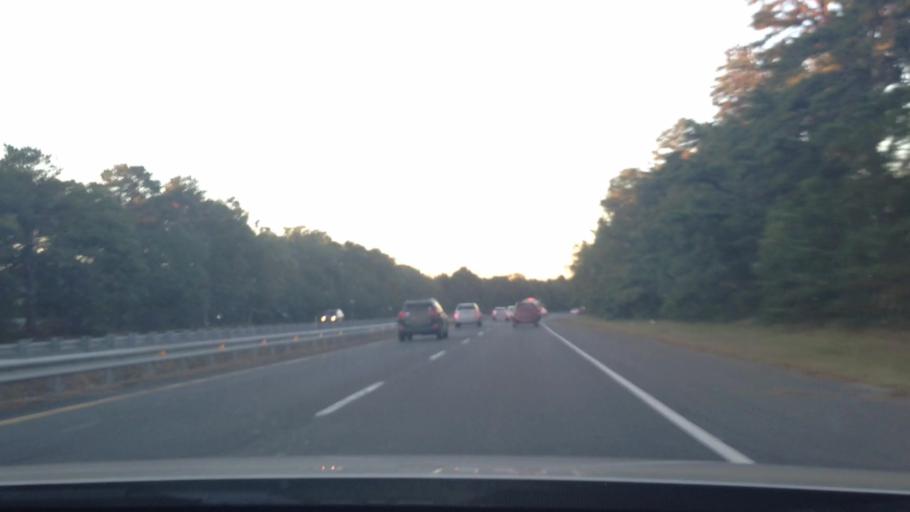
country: US
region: New York
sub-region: Suffolk County
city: Coram
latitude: 40.8880
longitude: -73.0082
